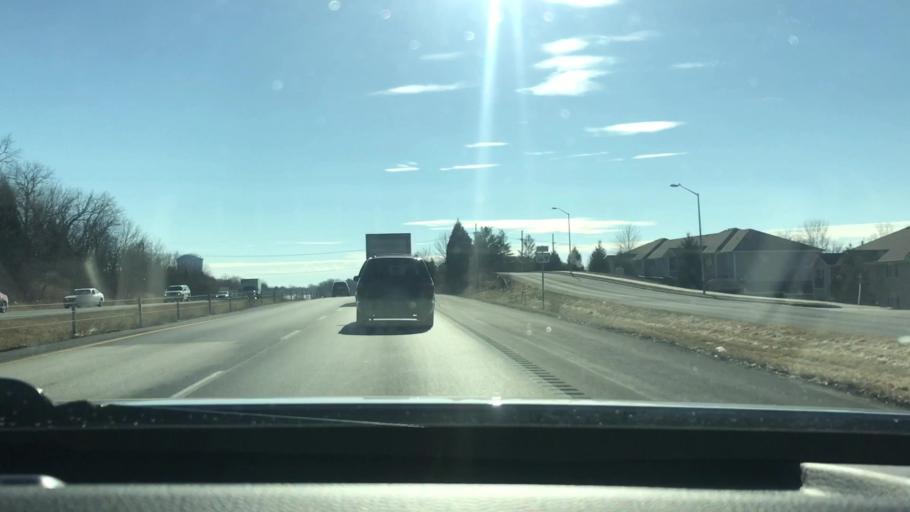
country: US
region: Missouri
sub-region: Clay County
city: Gladstone
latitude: 39.2409
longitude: -94.5905
